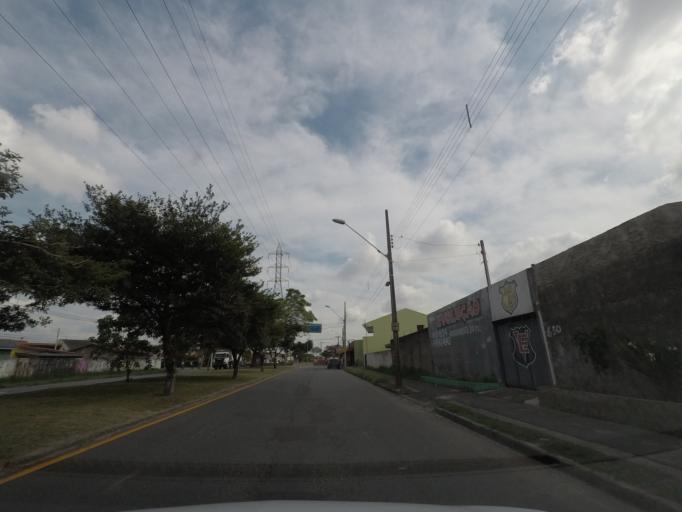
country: BR
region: Parana
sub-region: Pinhais
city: Pinhais
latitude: -25.4677
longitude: -49.1990
